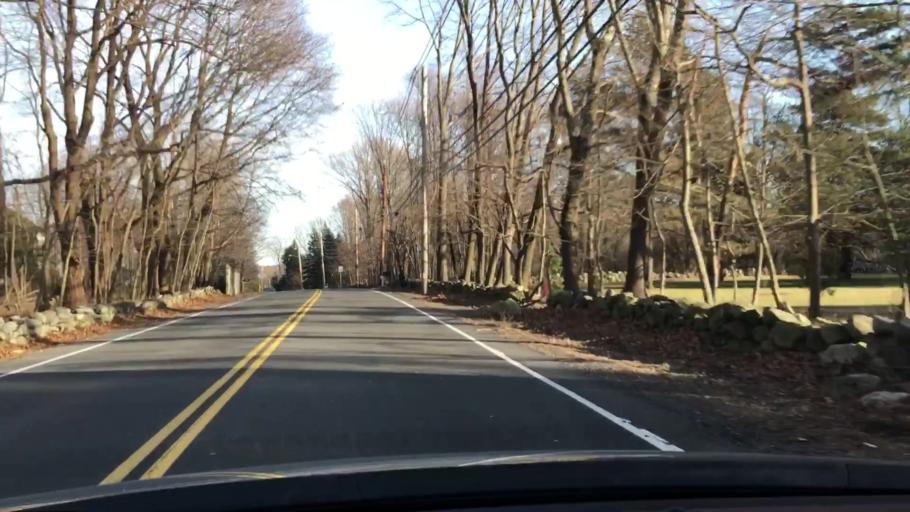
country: US
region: Massachusetts
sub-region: Norfolk County
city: Westwood
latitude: 42.2211
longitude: -71.2066
